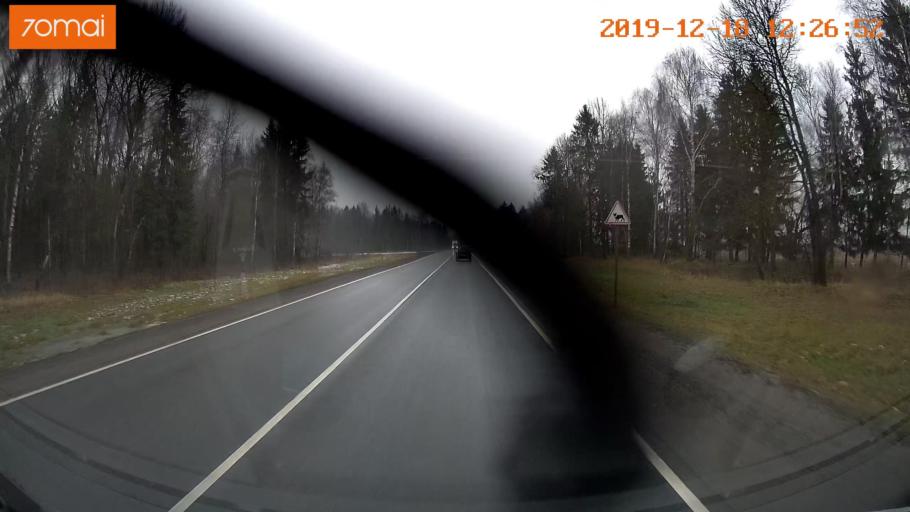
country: RU
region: Moskovskaya
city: Novopetrovskoye
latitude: 56.0559
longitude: 36.5023
